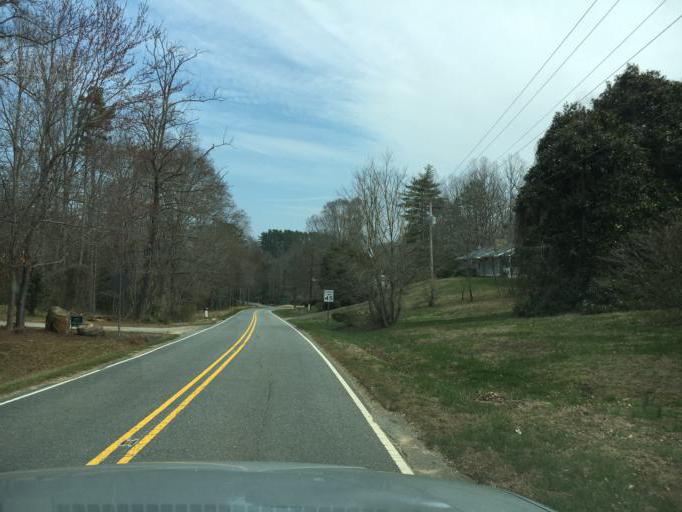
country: US
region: North Carolina
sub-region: Rutherford County
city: Lake Lure
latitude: 35.4492
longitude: -82.1456
